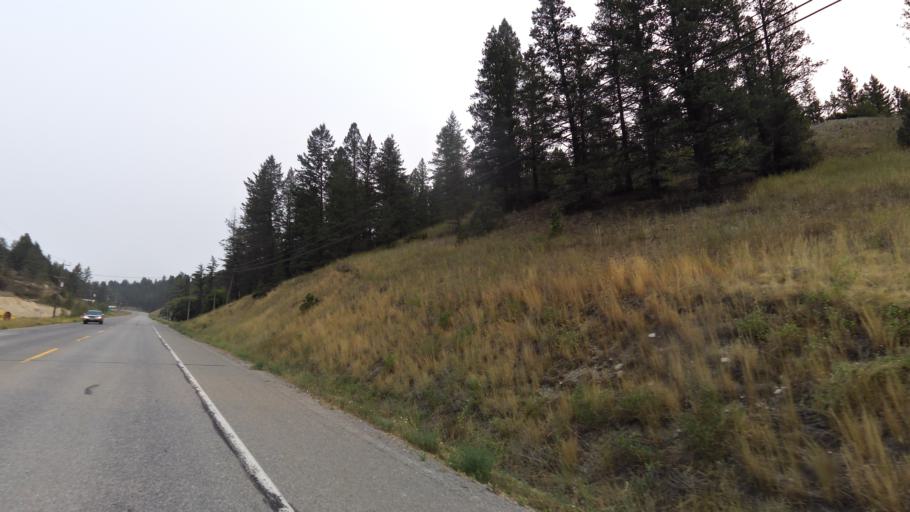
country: CA
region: British Columbia
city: Invermere
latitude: 50.5886
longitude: -116.0429
